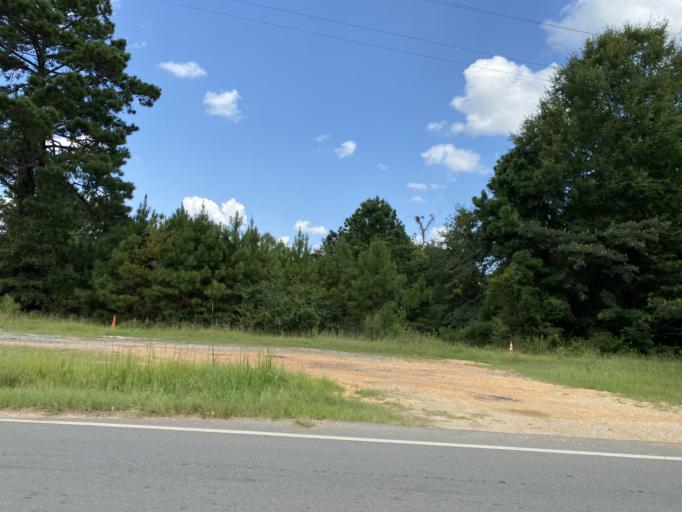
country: US
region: Alabama
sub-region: Wilcox County
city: Camden
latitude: 31.9970
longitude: -87.2785
